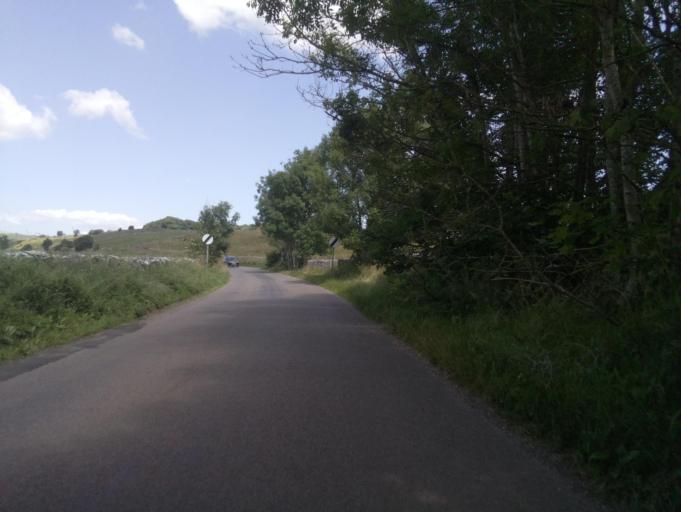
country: GB
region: England
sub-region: Derbyshire
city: Tideswell
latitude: 53.2009
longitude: -1.7771
